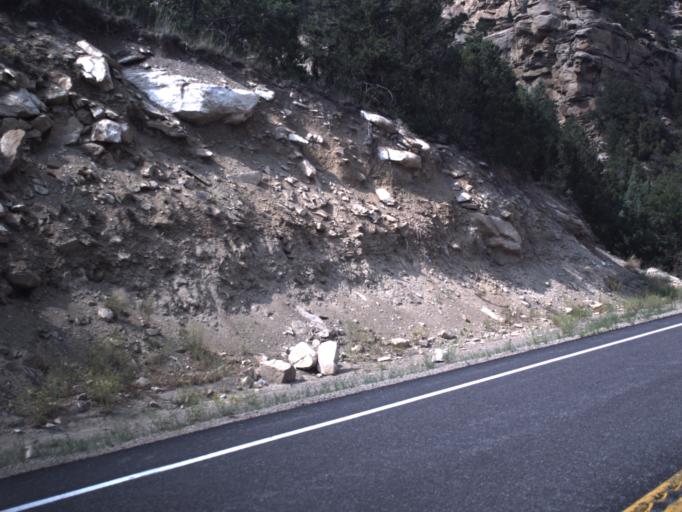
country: US
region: Utah
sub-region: Carbon County
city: Helper
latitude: 39.7555
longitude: -110.8240
